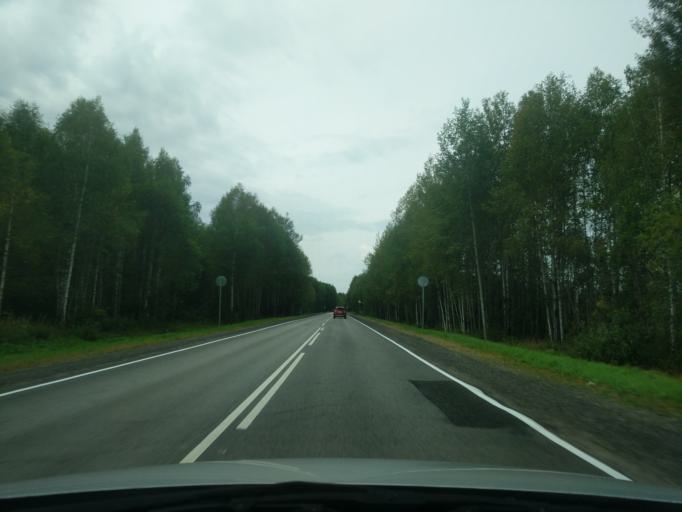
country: RU
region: Kirov
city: Kotel'nich
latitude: 58.2724
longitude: 48.1109
